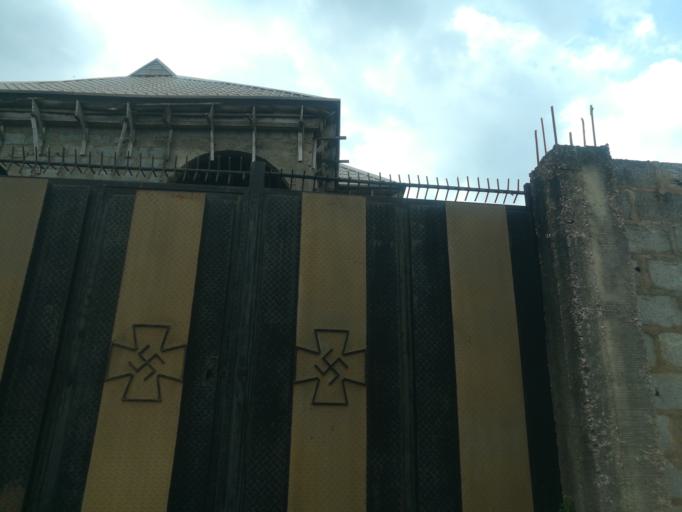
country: NG
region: Oyo
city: Ibadan
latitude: 7.4403
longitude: 3.9457
